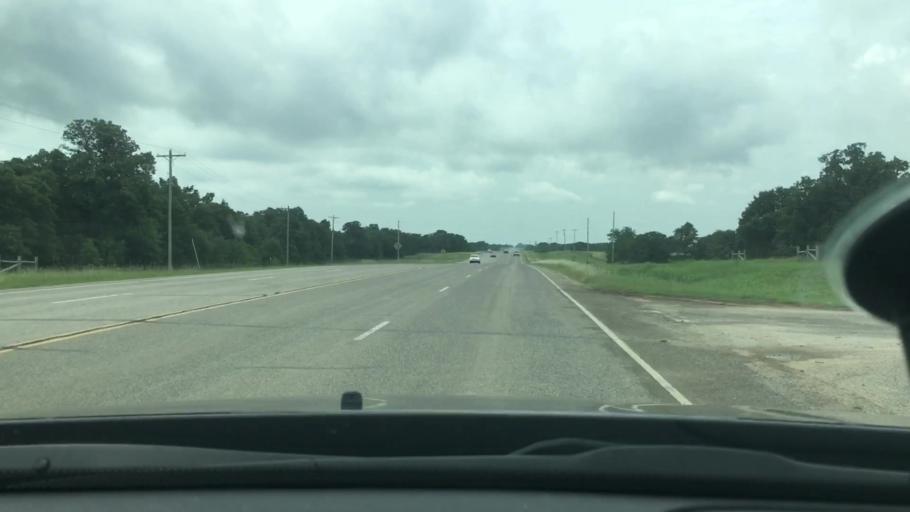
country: US
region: Oklahoma
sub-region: Carter County
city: Healdton
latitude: 34.1965
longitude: -97.4748
